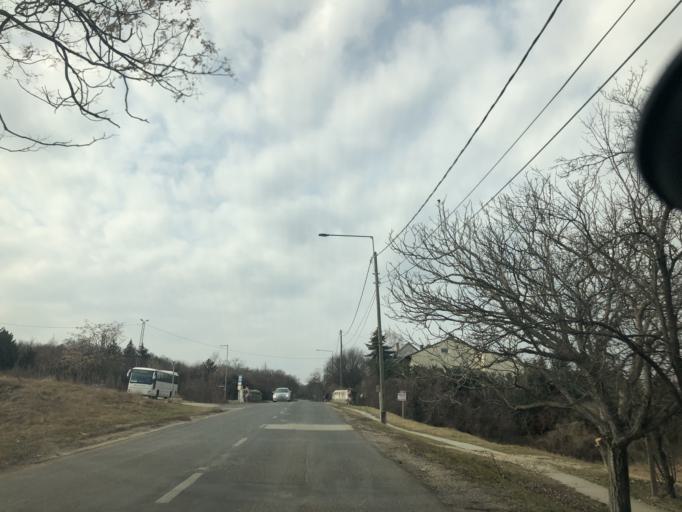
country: HU
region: Fejer
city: Etyek
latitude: 47.4444
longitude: 18.7437
